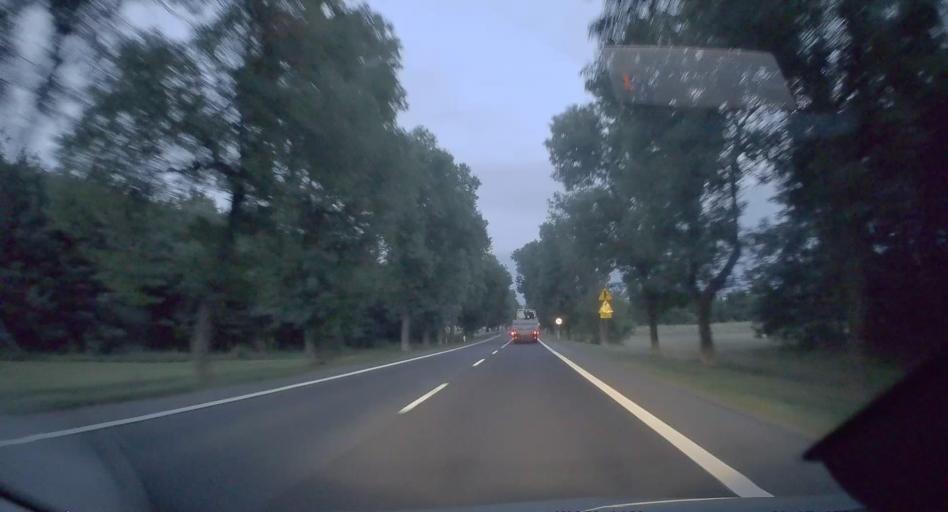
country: PL
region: Silesian Voivodeship
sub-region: Powiat klobucki
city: Klobuck
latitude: 50.9210
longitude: 18.8804
